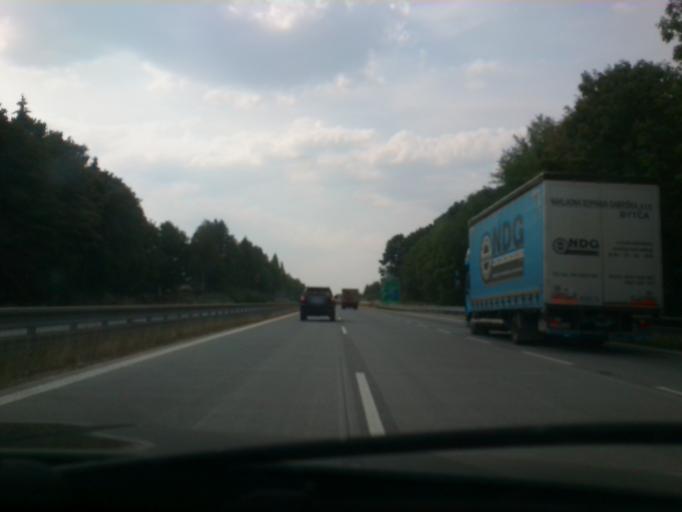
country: CZ
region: Central Bohemia
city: Divisov
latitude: 49.7988
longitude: 14.9152
